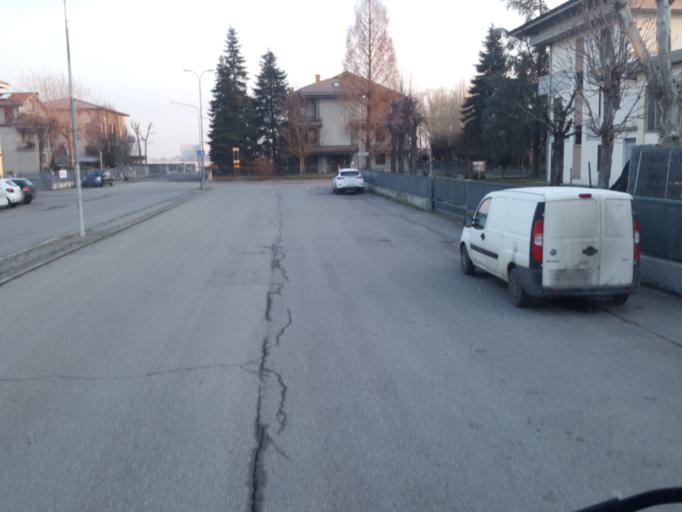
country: IT
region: Emilia-Romagna
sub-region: Provincia di Parma
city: Sorbolo
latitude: 44.8549
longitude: 10.4495
